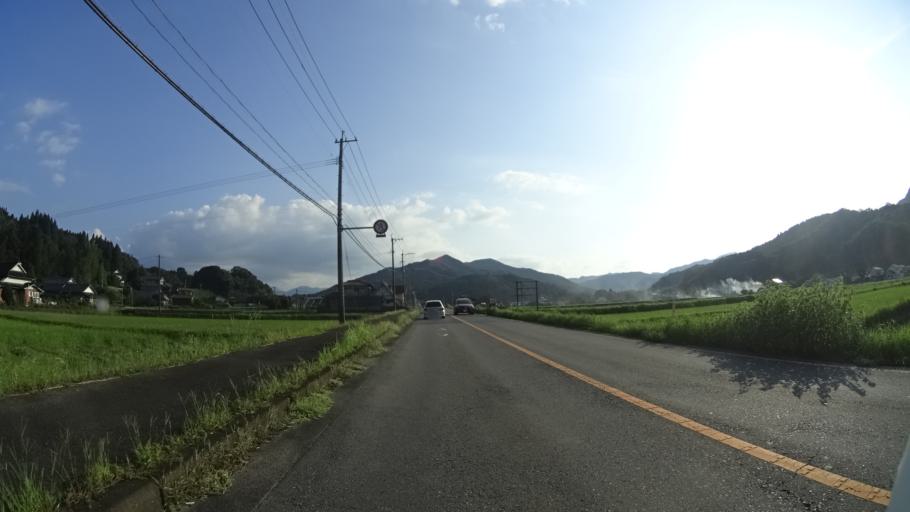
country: JP
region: Oita
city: Bungo-Takada-shi
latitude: 33.4579
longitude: 131.3298
